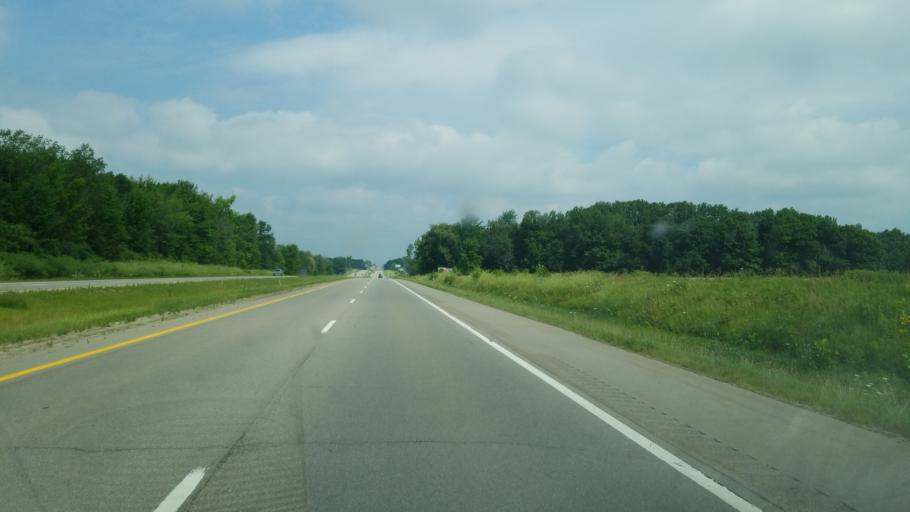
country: US
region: Michigan
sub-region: Kent County
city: Comstock Park
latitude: 43.0959
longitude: -85.6928
